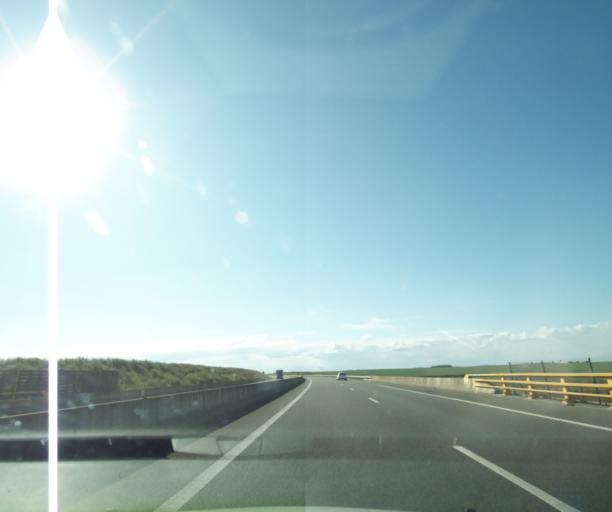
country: FR
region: Centre
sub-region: Departement d'Eure-et-Loir
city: Voves
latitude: 48.2689
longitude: 1.7547
